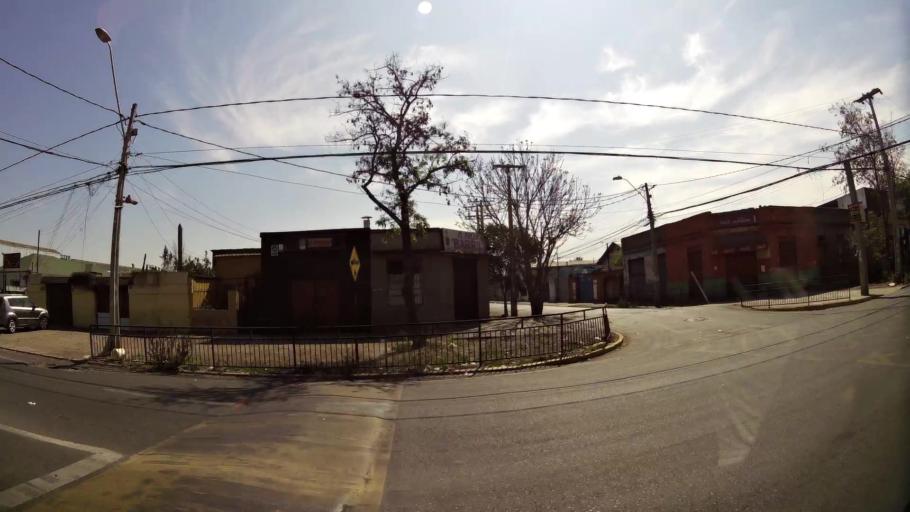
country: CL
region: Santiago Metropolitan
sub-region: Provincia de Santiago
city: Santiago
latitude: -33.4033
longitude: -70.6553
